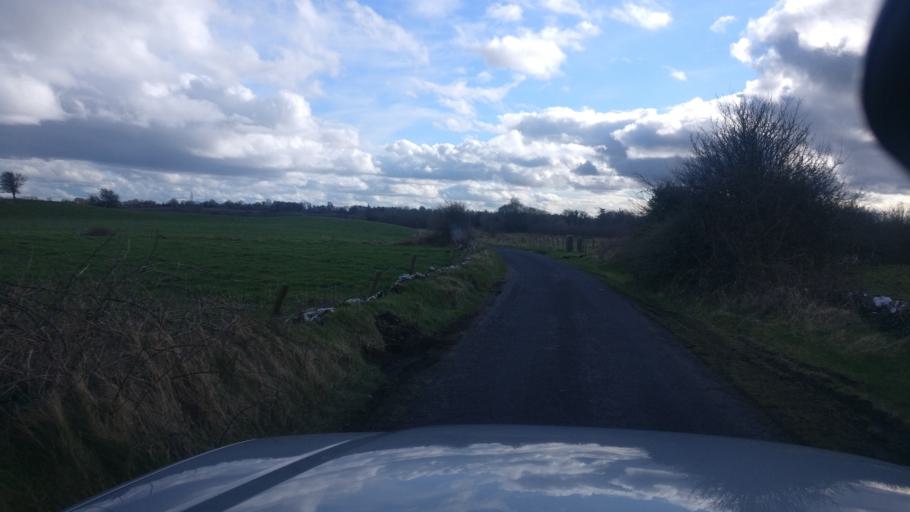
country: IE
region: Connaught
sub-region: County Galway
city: Loughrea
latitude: 53.1970
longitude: -8.4296
